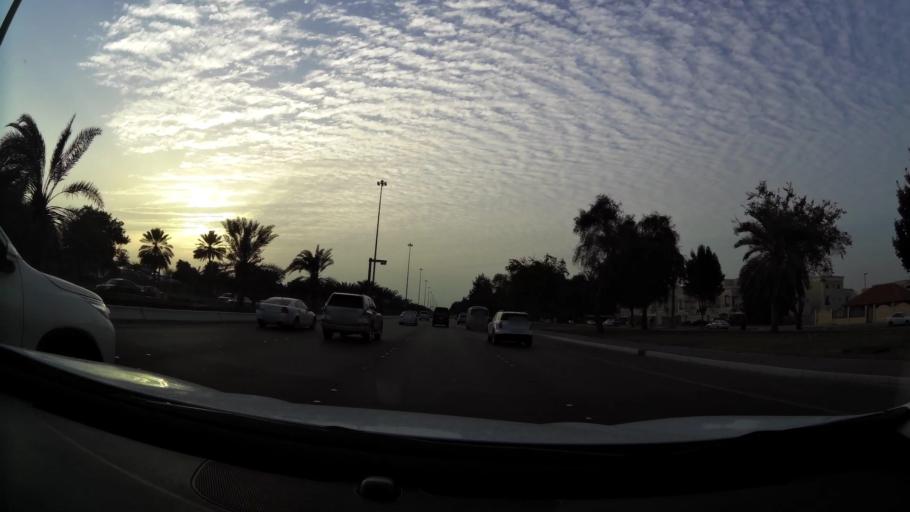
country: AE
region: Abu Dhabi
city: Abu Dhabi
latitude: 24.4263
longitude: 54.4043
